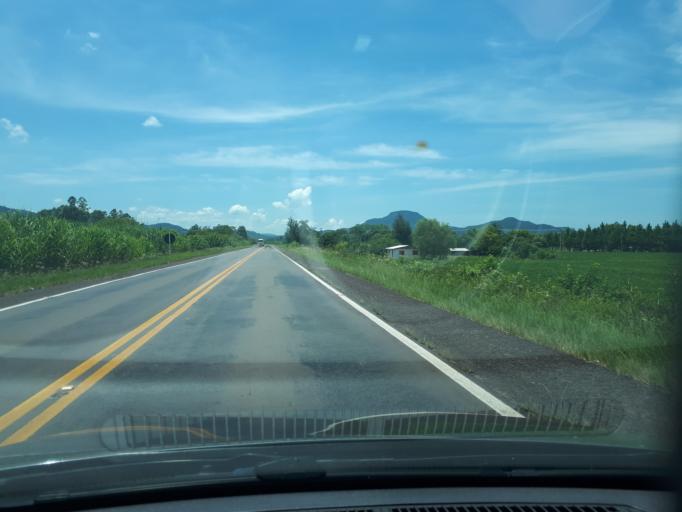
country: BR
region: Rio Grande do Sul
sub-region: Candelaria
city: Candelaria
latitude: -29.7236
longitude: -52.9200
